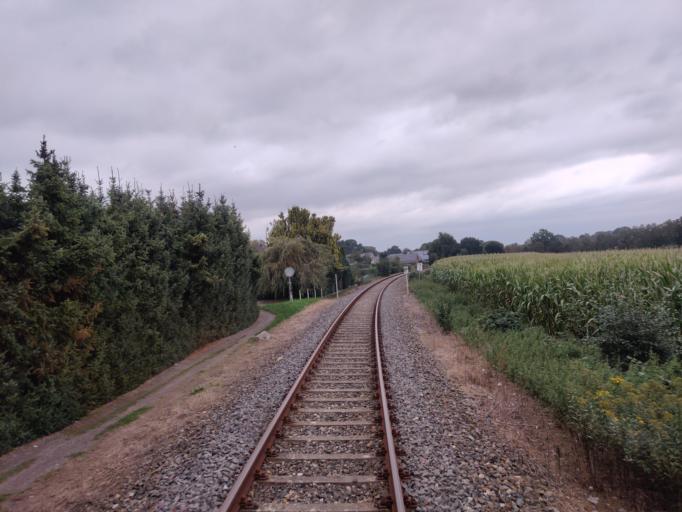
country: DE
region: Lower Saxony
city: Gnarrenburg
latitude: 53.3827
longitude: 9.0083
